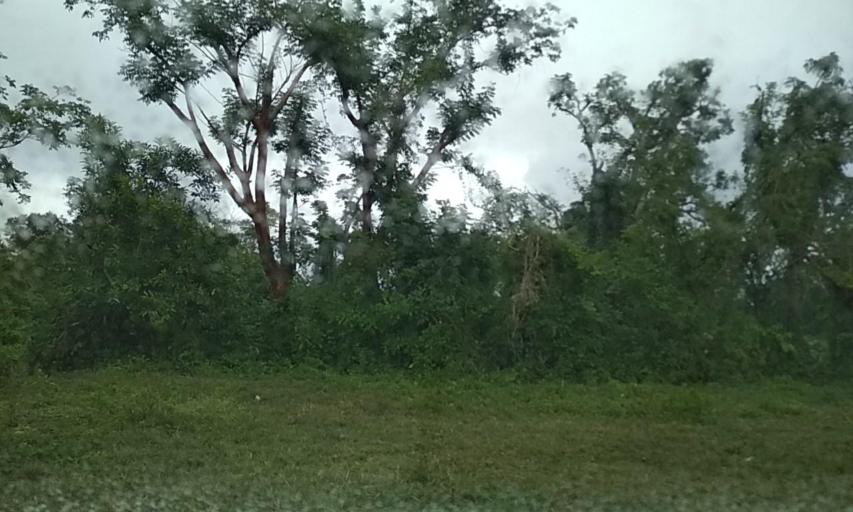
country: MX
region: Veracruz
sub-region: Papantla
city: El Chote
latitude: 20.3768
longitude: -97.3470
